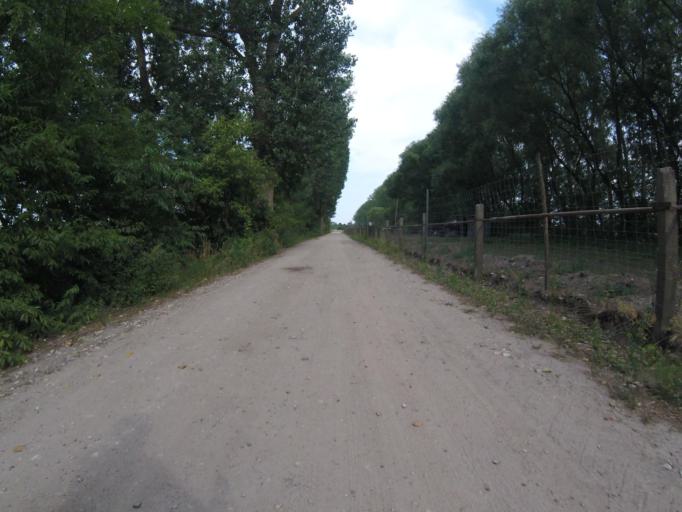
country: DE
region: Brandenburg
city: Erkner
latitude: 52.3057
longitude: 13.7722
